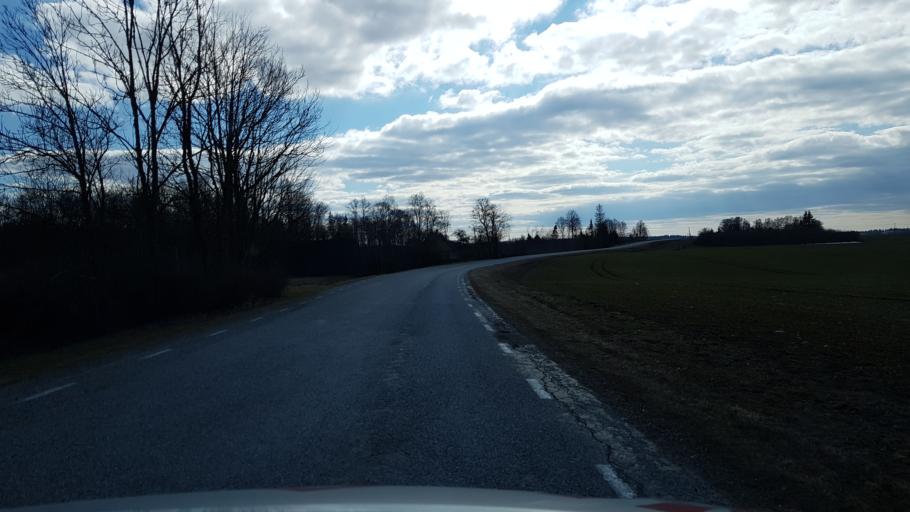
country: EE
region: Laeaene-Virumaa
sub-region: Kadrina vald
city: Kadrina
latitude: 59.2970
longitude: 26.2139
